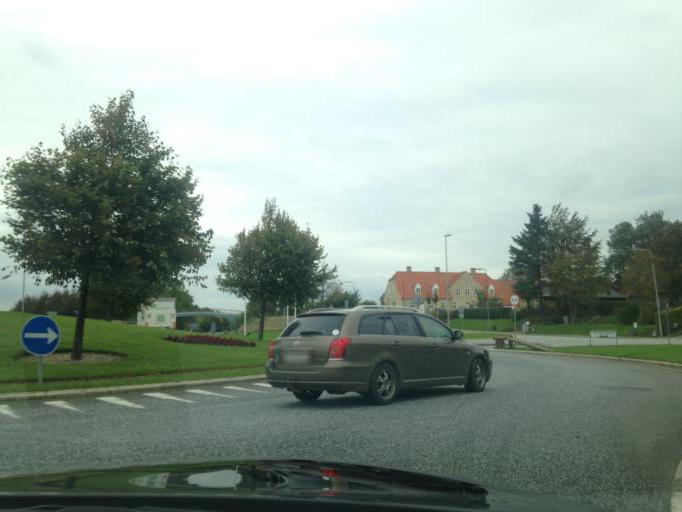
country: DK
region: South Denmark
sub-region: Kolding Kommune
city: Christiansfeld
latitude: 55.3539
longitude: 9.4772
